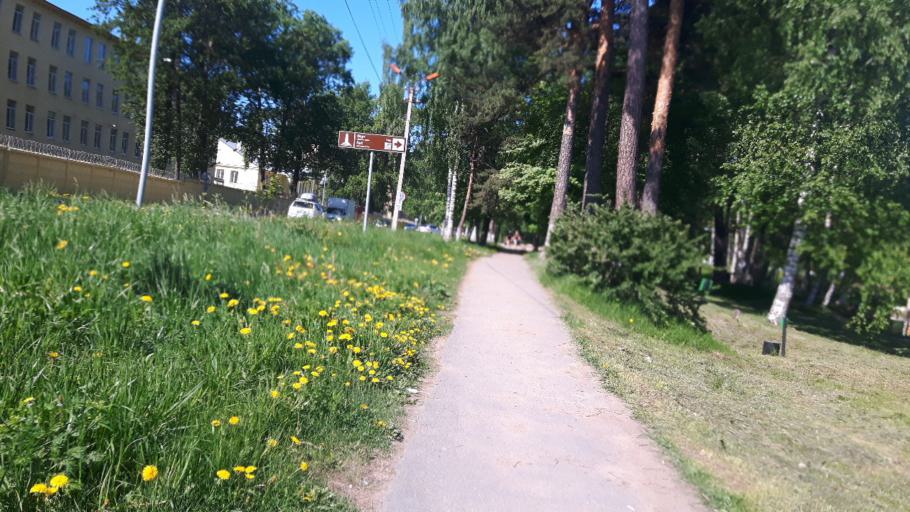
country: RU
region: Leningrad
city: Lebyazh'ye
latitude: 59.9614
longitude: 29.4170
